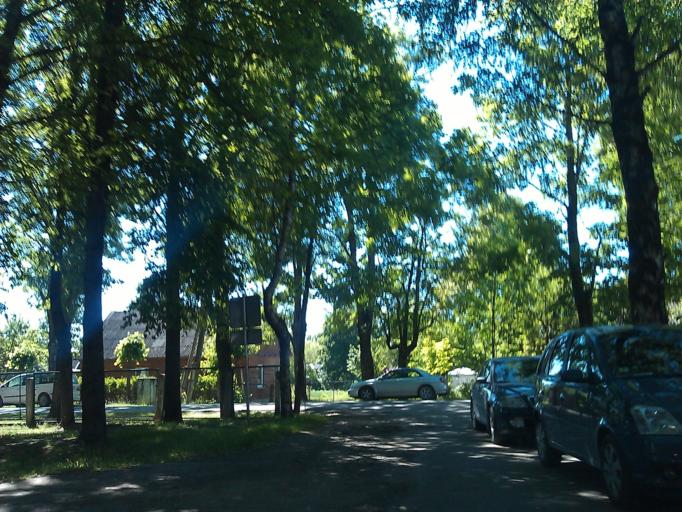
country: LV
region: Vilanu
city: Vilani
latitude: 56.5508
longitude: 26.9250
